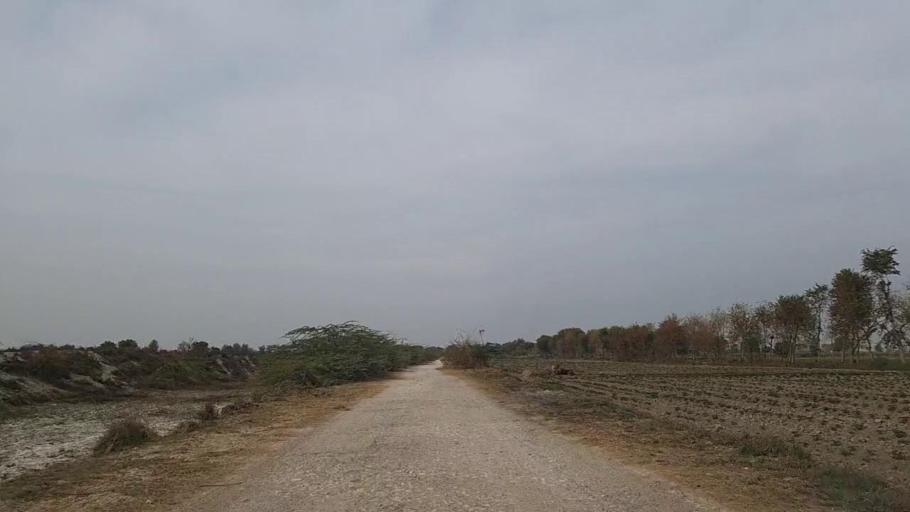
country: PK
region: Sindh
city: Daur
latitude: 26.4208
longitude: 68.4203
